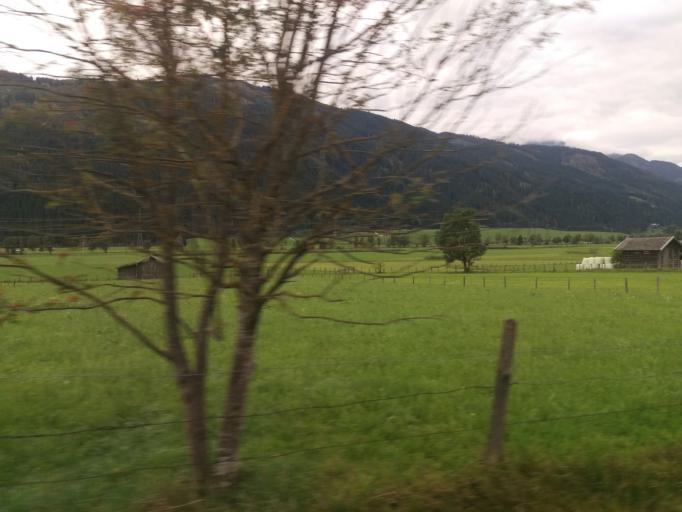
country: AT
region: Salzburg
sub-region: Politischer Bezirk Zell am See
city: Uttendorf
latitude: 47.2846
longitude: 12.5572
